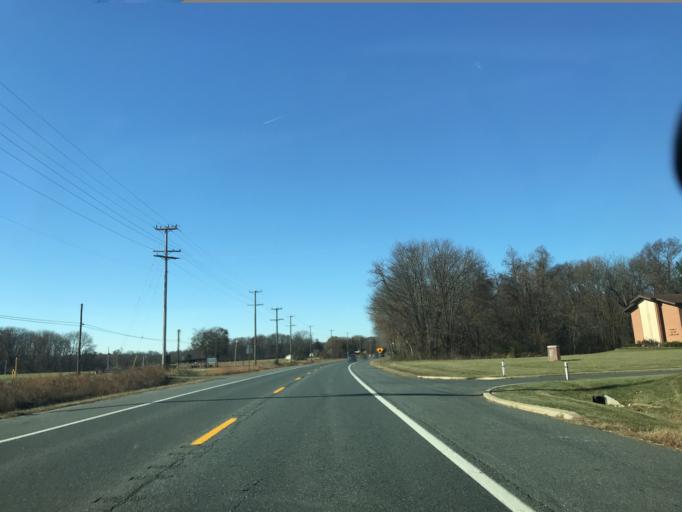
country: US
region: Maryland
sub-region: Harford County
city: Aberdeen
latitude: 39.5730
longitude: -76.1782
